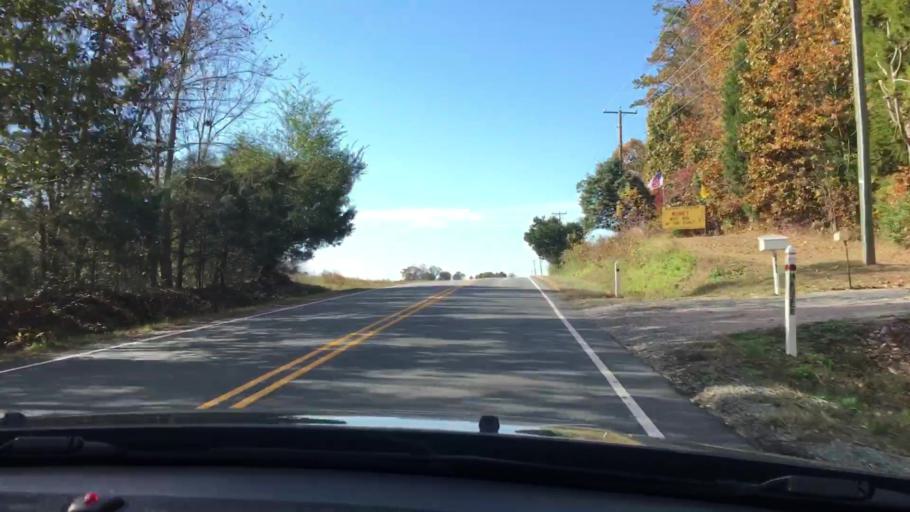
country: US
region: Virginia
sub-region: King and Queen County
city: King and Queen Court House
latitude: 37.5910
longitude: -76.8844
